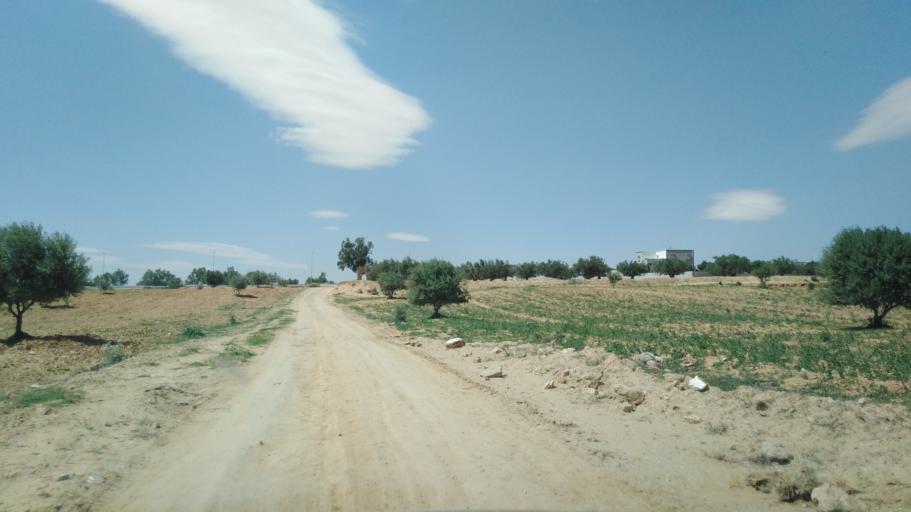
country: TN
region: Safaqis
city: Sfax
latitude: 34.7625
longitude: 10.5166
